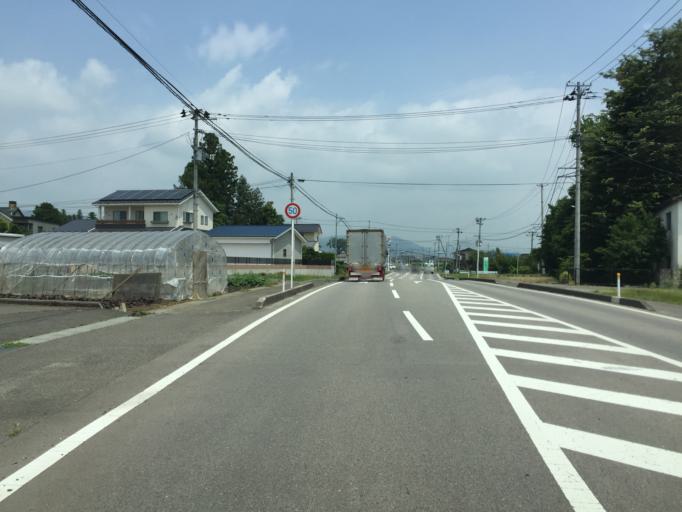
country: JP
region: Fukushima
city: Fukushima-shi
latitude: 37.7573
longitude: 140.4019
